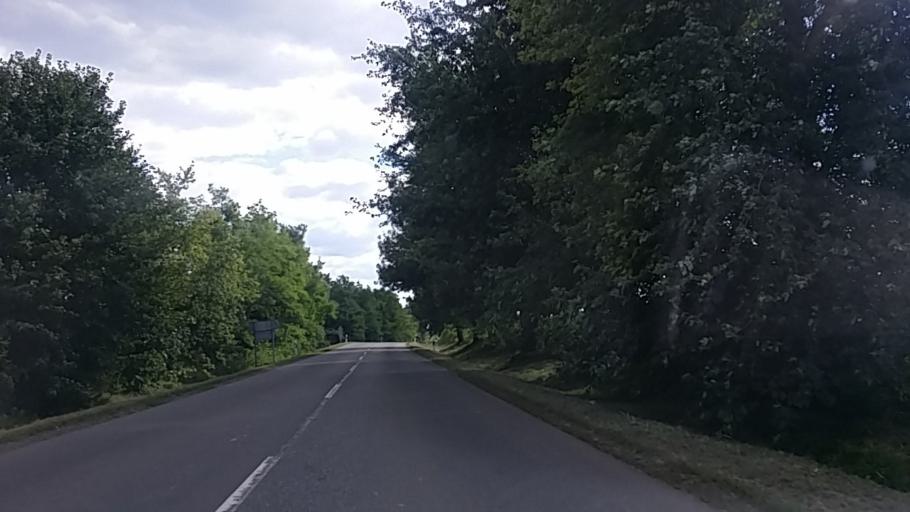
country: HU
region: Baranya
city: Sasd
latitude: 46.2895
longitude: 18.1205
